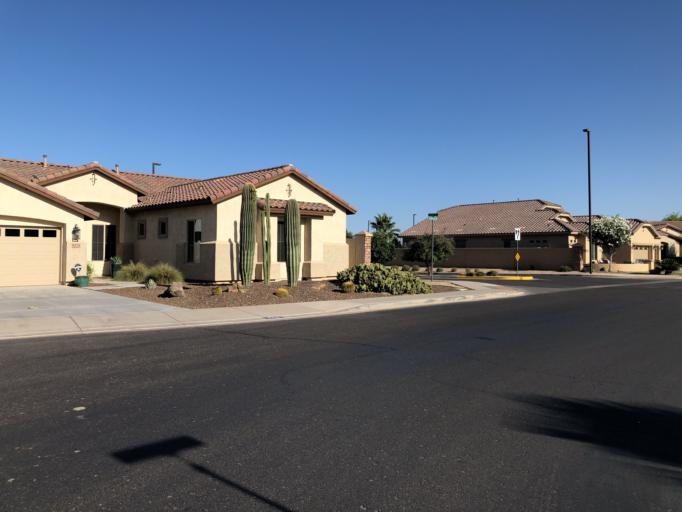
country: US
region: Arizona
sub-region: Maricopa County
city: Queen Creek
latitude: 33.2277
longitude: -111.7168
